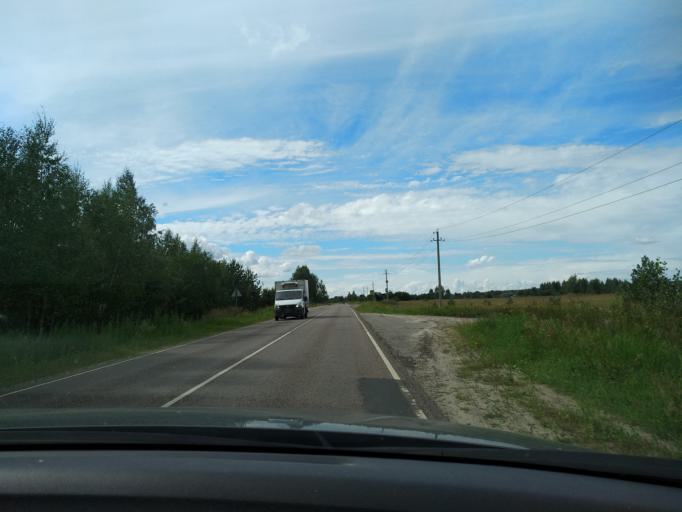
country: RU
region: Moskovskaya
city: Krasnyy Tkach
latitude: 55.3903
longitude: 39.1706
